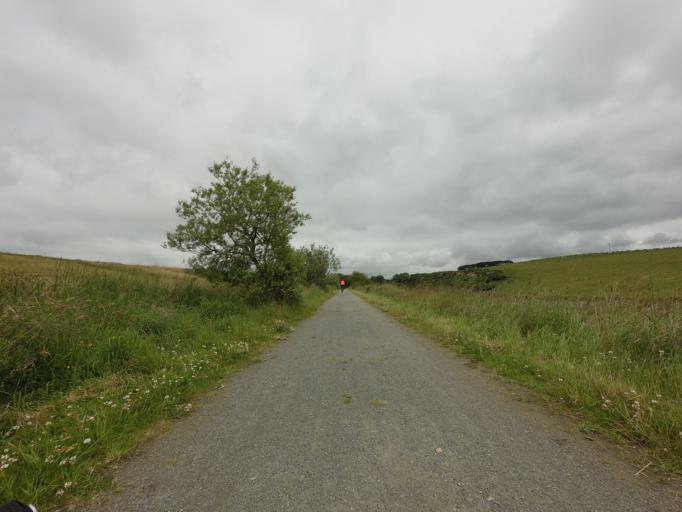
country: GB
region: Scotland
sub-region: Aberdeenshire
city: Mintlaw
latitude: 57.5157
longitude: -2.1348
